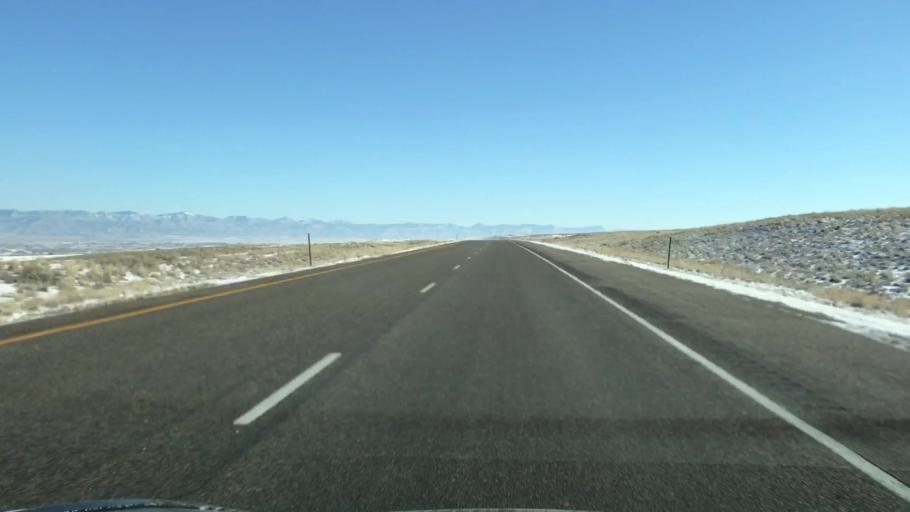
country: US
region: Colorado
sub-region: Mesa County
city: Loma
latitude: 39.2262
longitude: -108.9275
